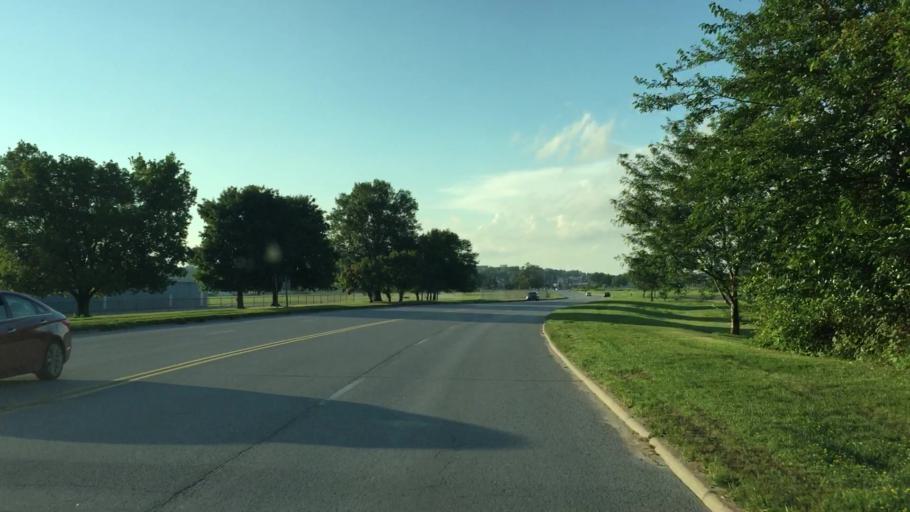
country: US
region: Iowa
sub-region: Johnson County
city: Iowa City
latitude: 41.6399
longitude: -91.5389
